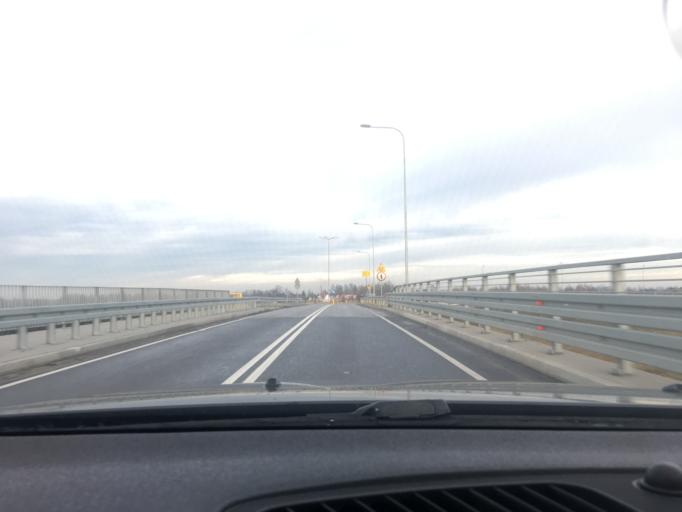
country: PL
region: Swietokrzyskie
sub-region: Powiat jedrzejowski
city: Sobkow
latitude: 50.6901
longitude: 20.3701
